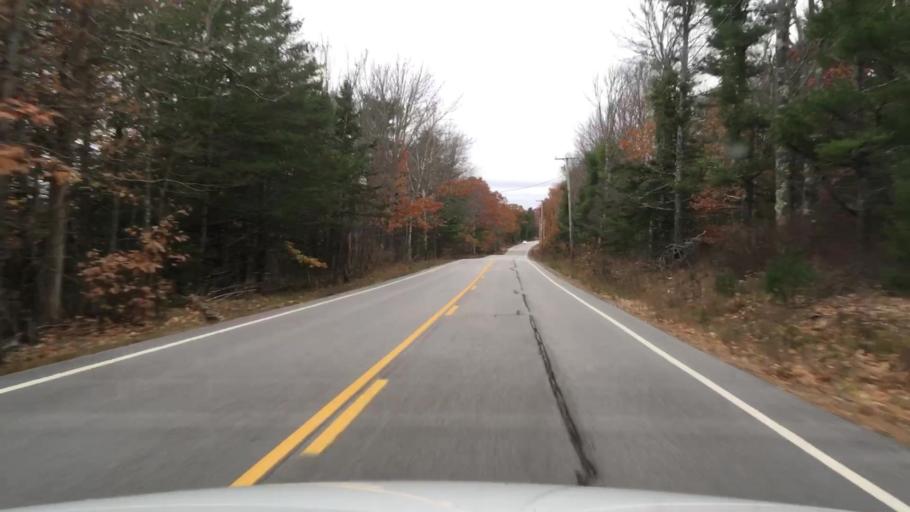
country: US
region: Maine
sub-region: Hancock County
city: Orland
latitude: 44.5393
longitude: -68.6818
